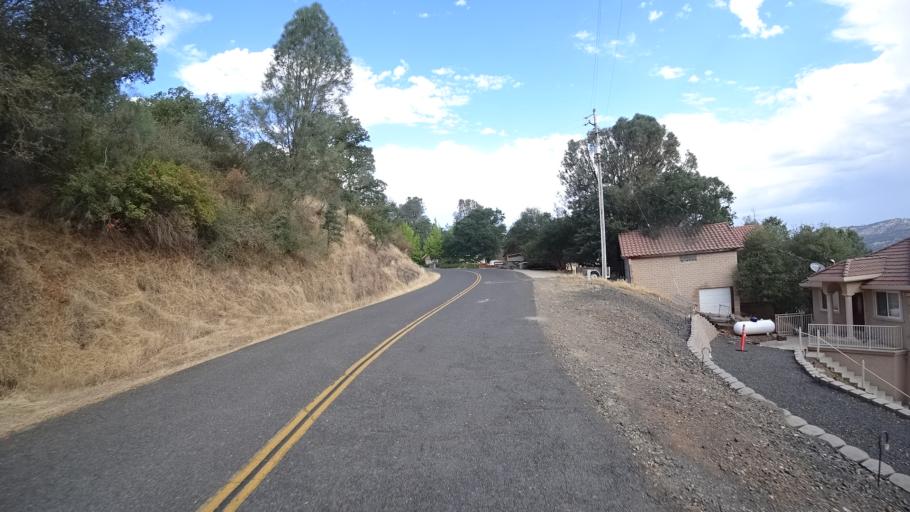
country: US
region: California
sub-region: Calaveras County
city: Copperopolis
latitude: 37.9076
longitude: -120.6001
